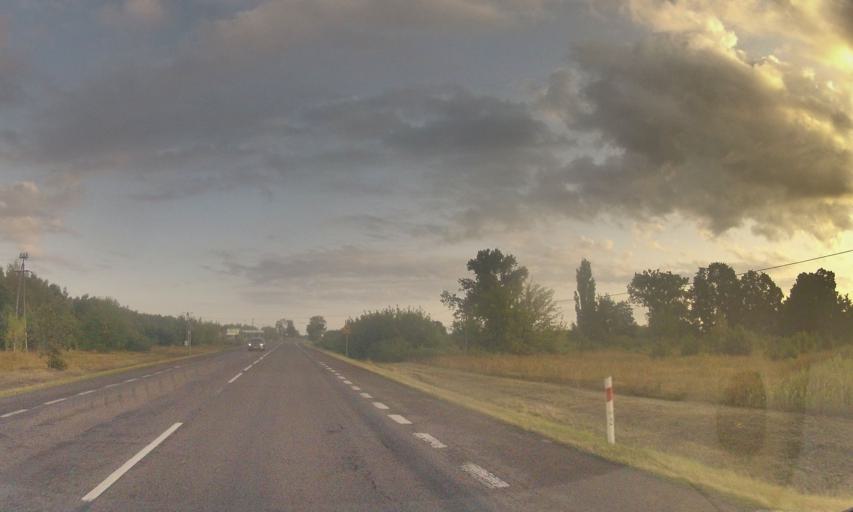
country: PL
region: Masovian Voivodeship
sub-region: Powiat ciechanowski
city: Glinojeck
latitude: 52.7760
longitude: 20.2904
